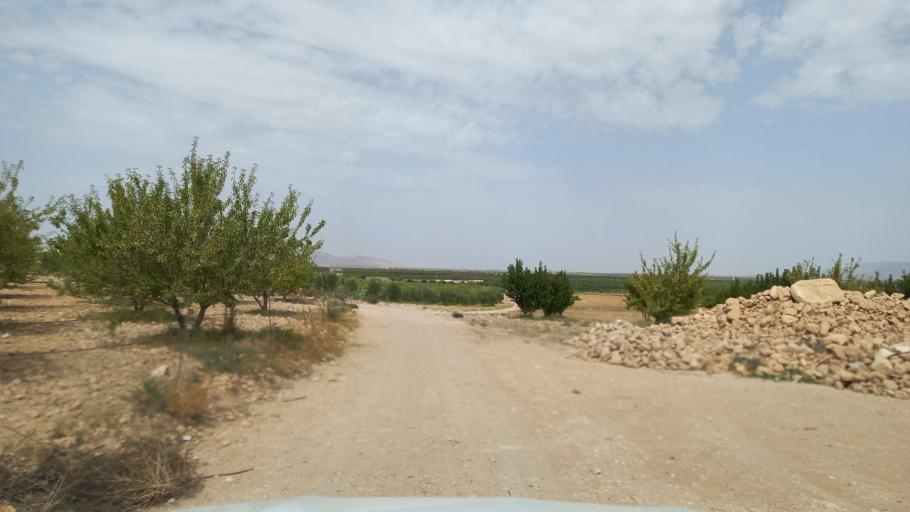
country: TN
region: Al Qasrayn
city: Kasserine
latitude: 35.2835
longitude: 9.0108
